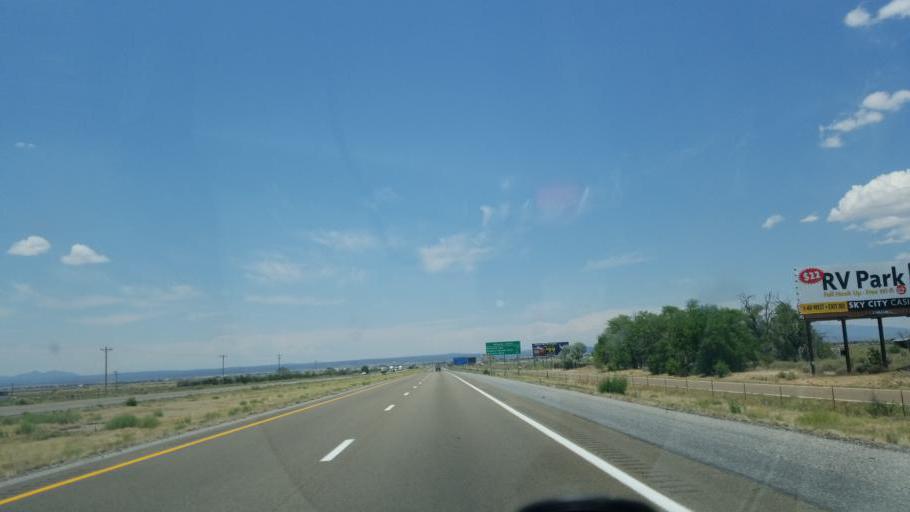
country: US
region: New Mexico
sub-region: Torrance County
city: Moriarty
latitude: 35.0049
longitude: -105.9762
